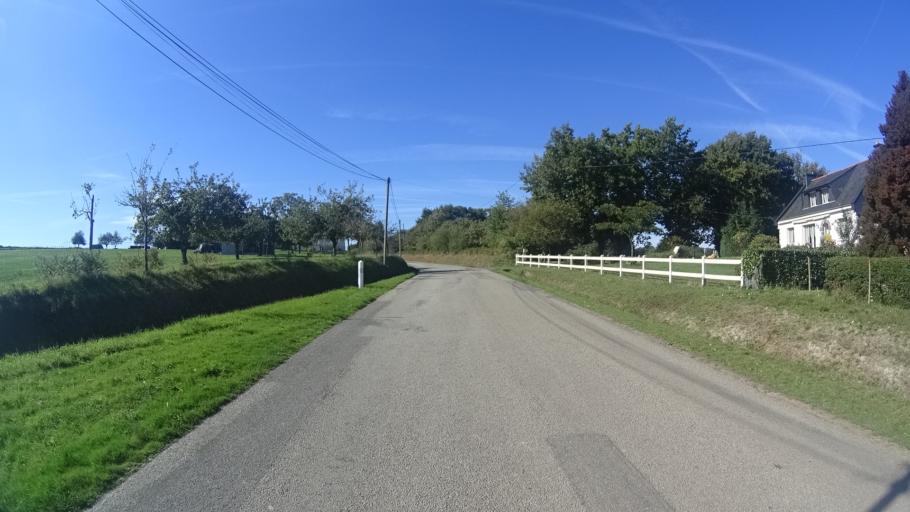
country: FR
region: Brittany
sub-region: Departement du Morbihan
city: Saint-Vincent-sur-Oust
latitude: 47.7292
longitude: -2.1637
